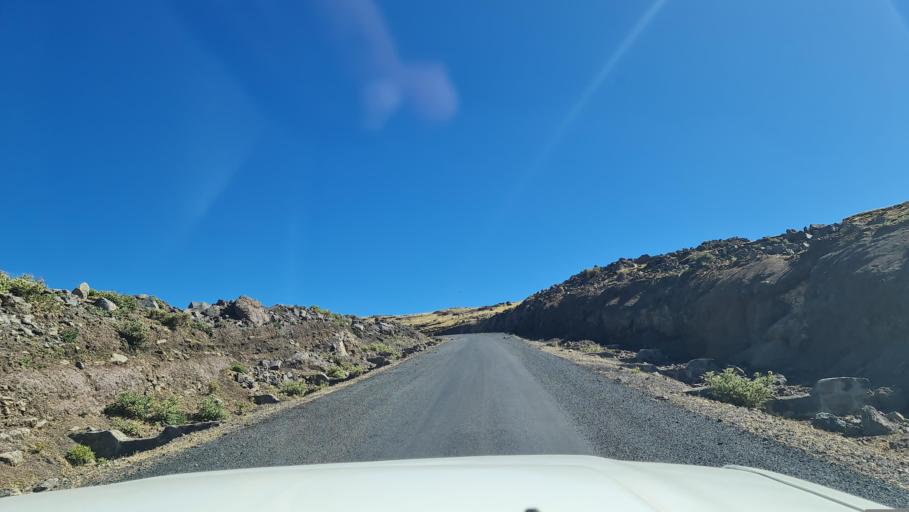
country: ET
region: Amhara
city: Debark'
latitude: 13.1492
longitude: 38.1859
